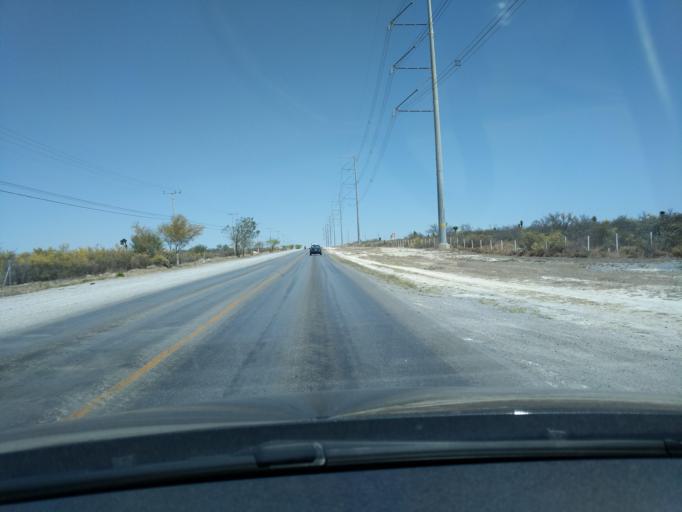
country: MX
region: Nuevo Leon
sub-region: Apodaca
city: Artemio Trevino
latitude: 25.8221
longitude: -100.1445
